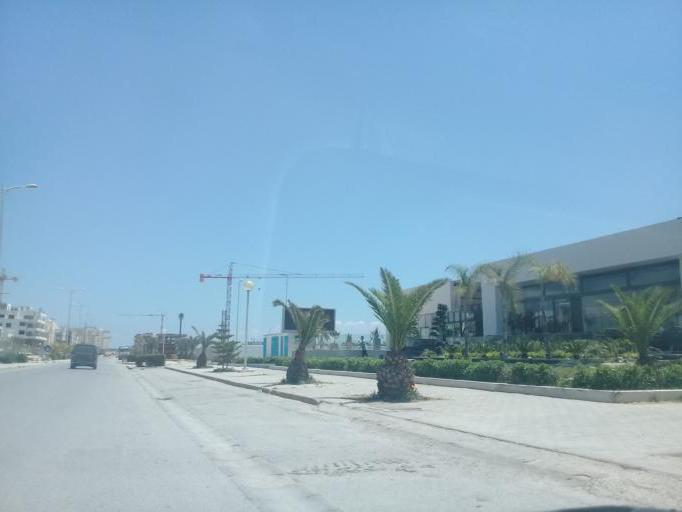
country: TN
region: Tunis
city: La Goulette
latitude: 36.8421
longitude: 10.2725
